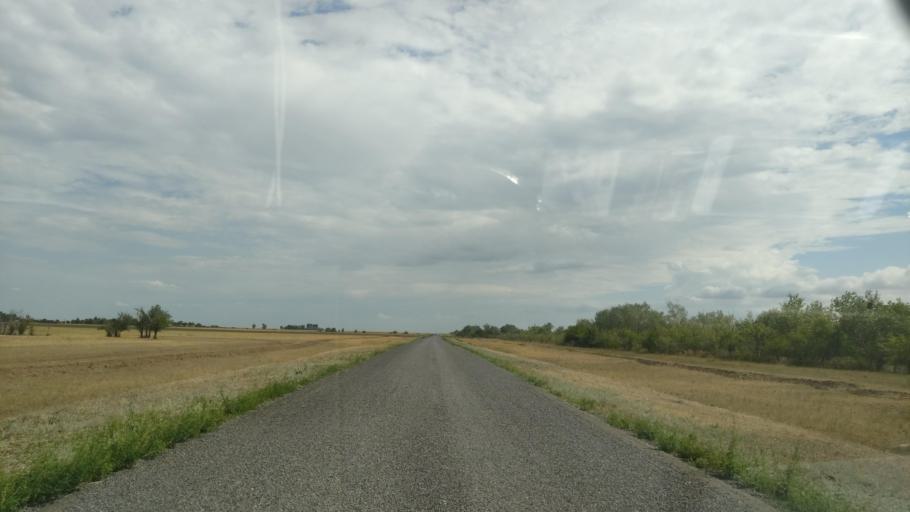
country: KZ
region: Pavlodar
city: Pavlodar
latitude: 52.6390
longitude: 77.0053
